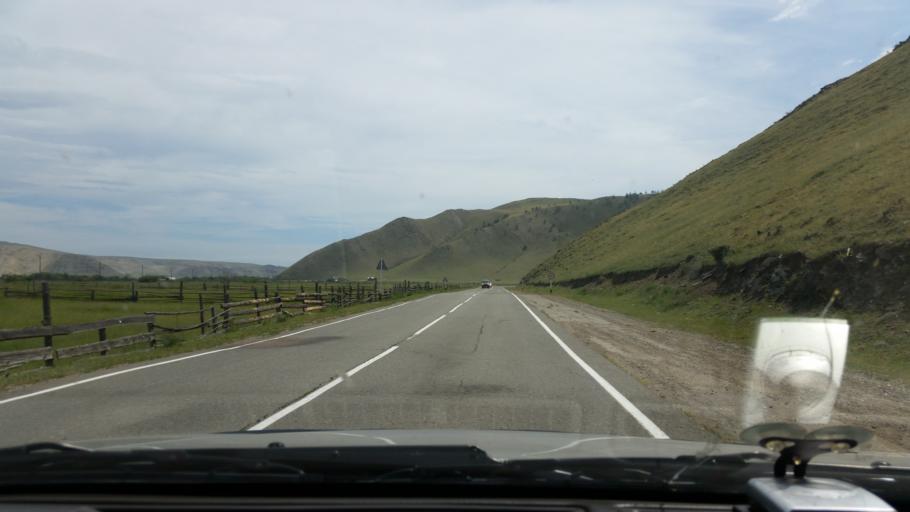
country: RU
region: Irkutsk
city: Yelantsy
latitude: 52.8064
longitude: 106.4664
